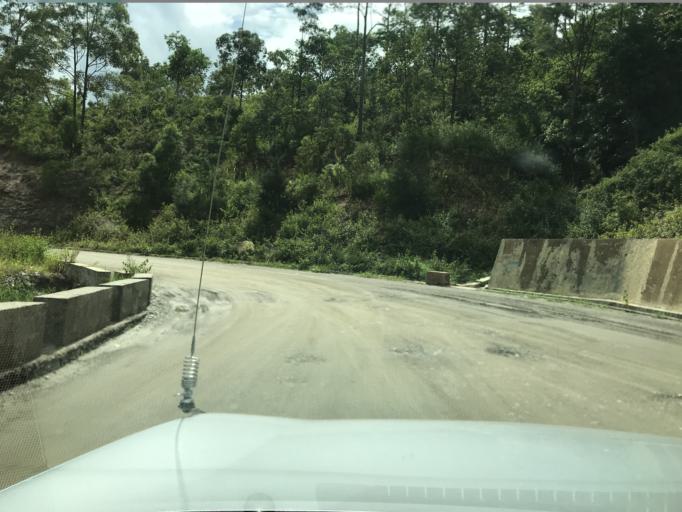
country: TL
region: Aileu
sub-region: Aileu Villa
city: Aileu
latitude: -8.6623
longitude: 125.5480
